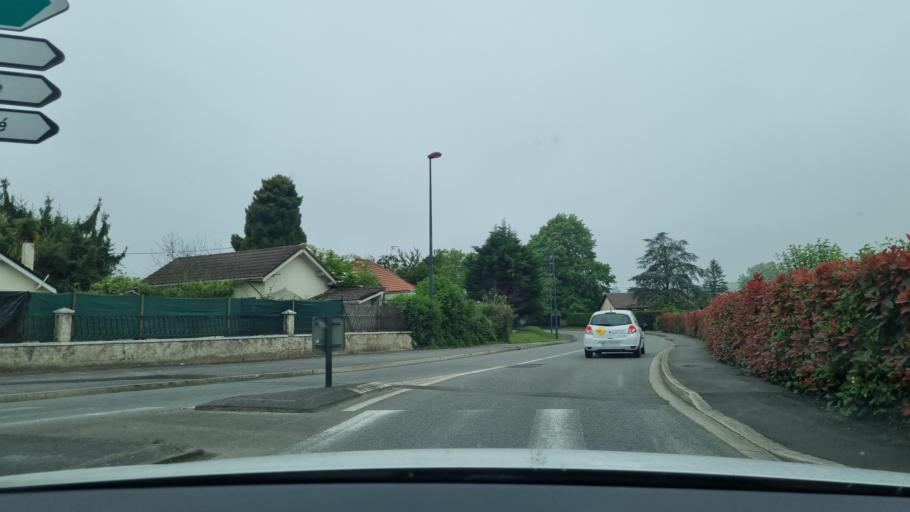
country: FR
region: Aquitaine
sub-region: Departement des Pyrenees-Atlantiques
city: Orthez
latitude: 43.4799
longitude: -0.7649
